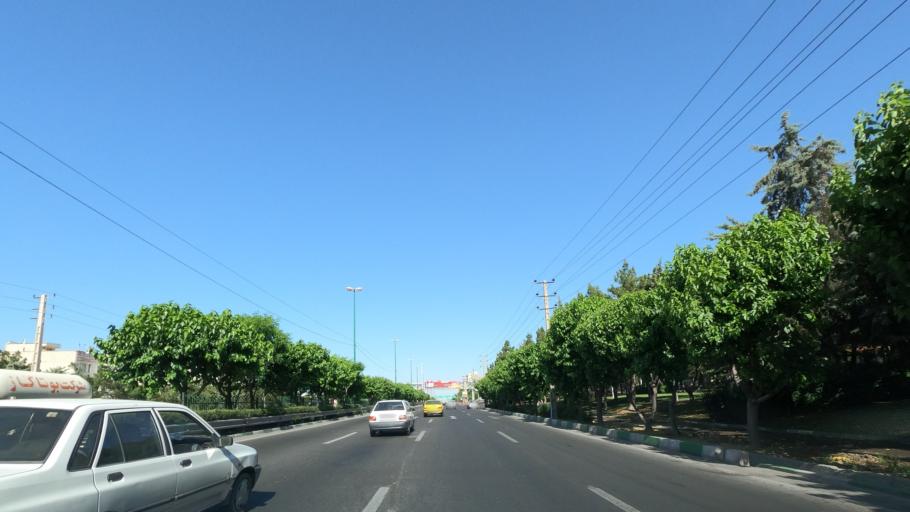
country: IR
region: Tehran
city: Tehran
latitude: 35.7533
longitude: 51.3061
